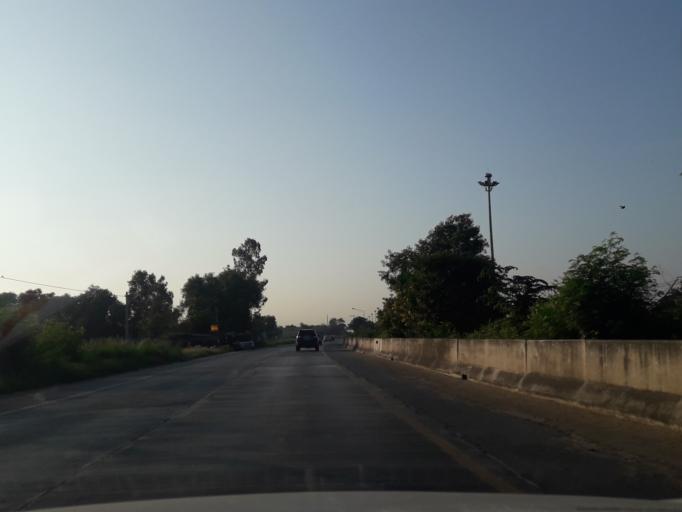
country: TH
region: Phra Nakhon Si Ayutthaya
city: Bang Pa-in
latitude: 14.1700
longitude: 100.5625
